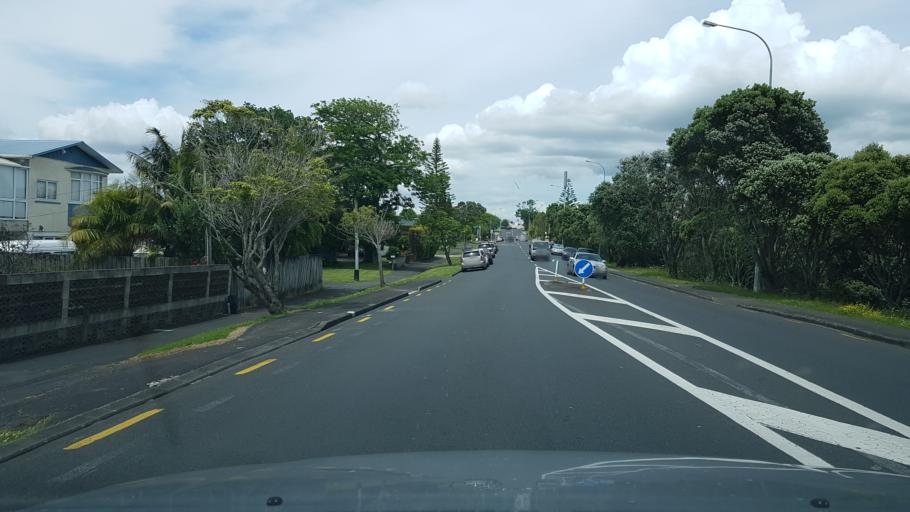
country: NZ
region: Auckland
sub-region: Auckland
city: North Shore
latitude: -36.8055
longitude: 174.7254
